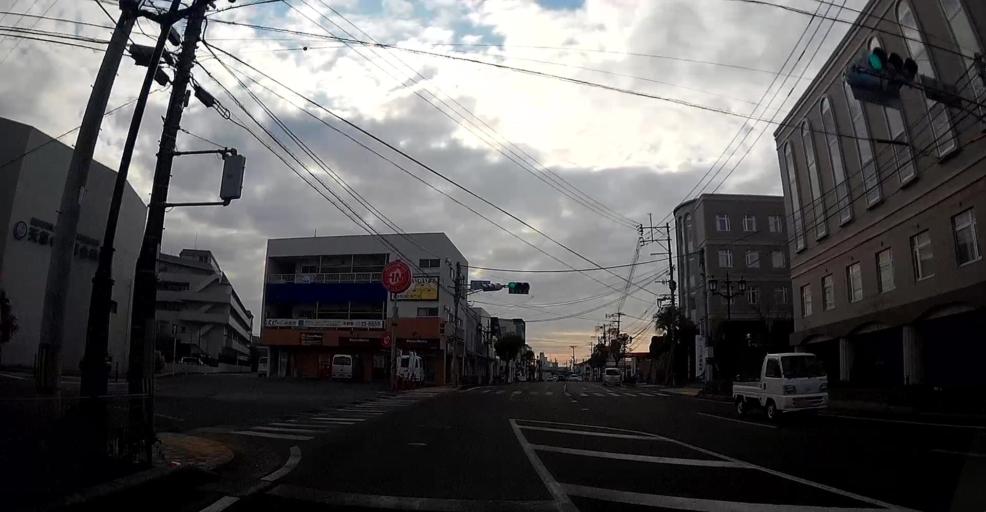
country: JP
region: Kumamoto
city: Hondo
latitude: 32.4496
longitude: 130.1992
